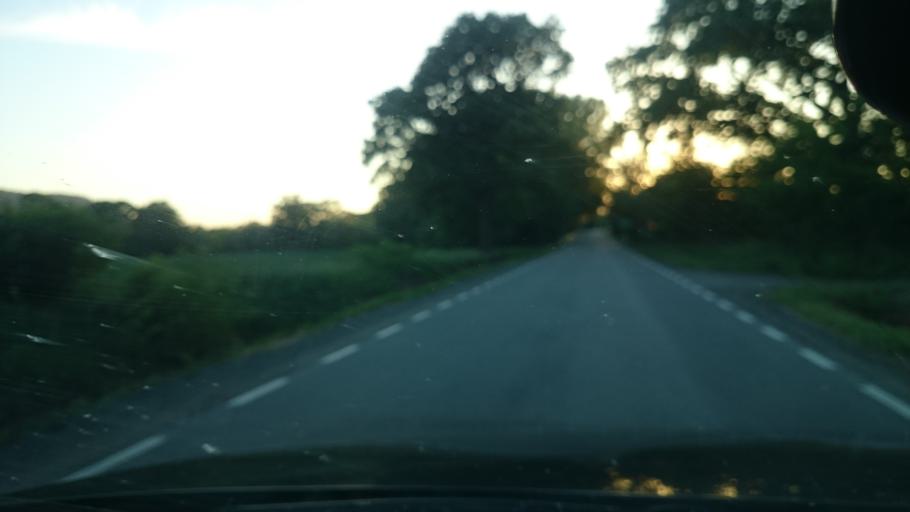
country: PL
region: Lower Silesian Voivodeship
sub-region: Powiat zabkowicki
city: Bardo
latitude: 50.5098
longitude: 16.7860
